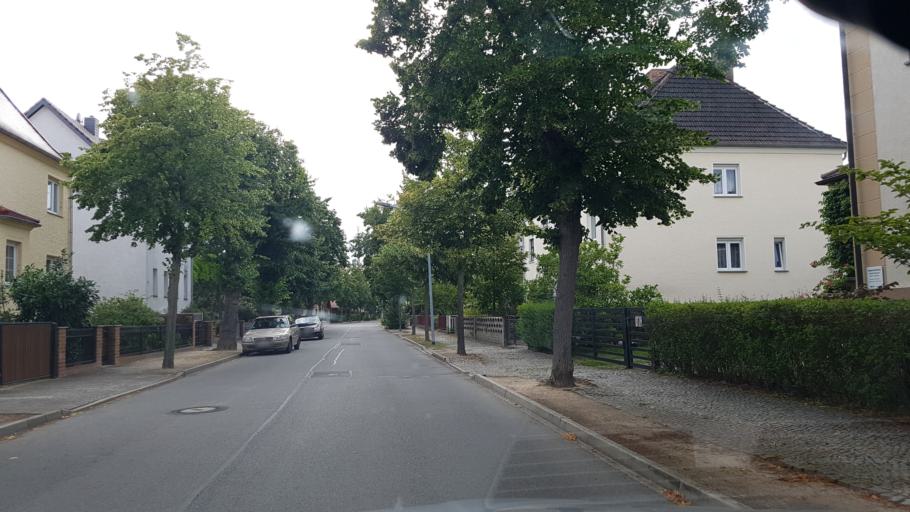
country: DE
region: Brandenburg
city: Falkenberg
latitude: 51.5825
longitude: 13.2313
